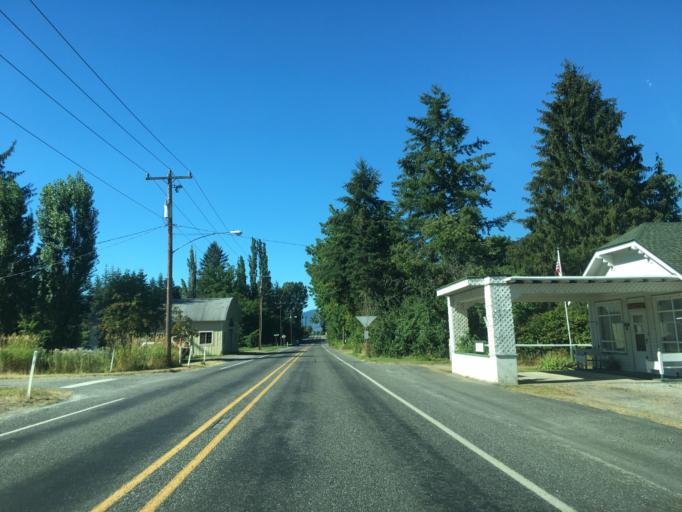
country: US
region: Washington
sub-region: Whatcom County
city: Sudden Valley
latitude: 48.7169
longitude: -122.2035
